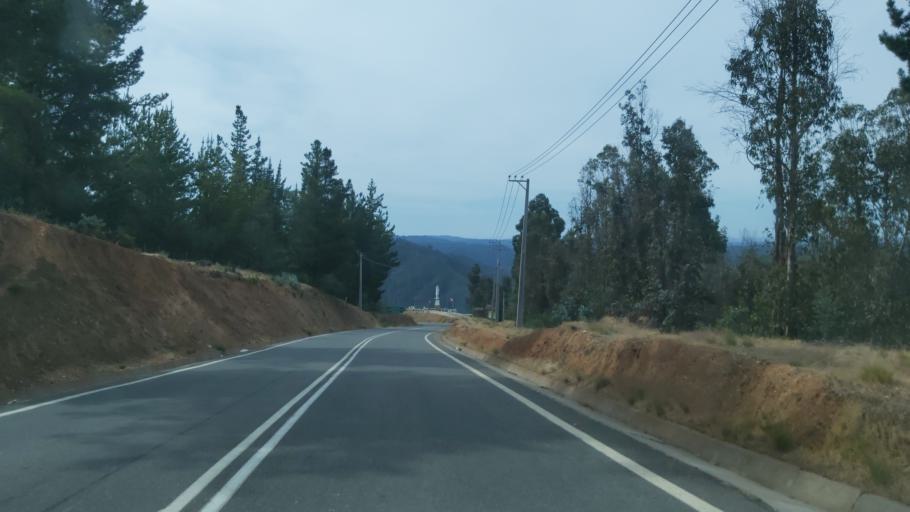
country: CL
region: Maule
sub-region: Provincia de Talca
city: Constitucion
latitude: -34.9129
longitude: -71.9958
